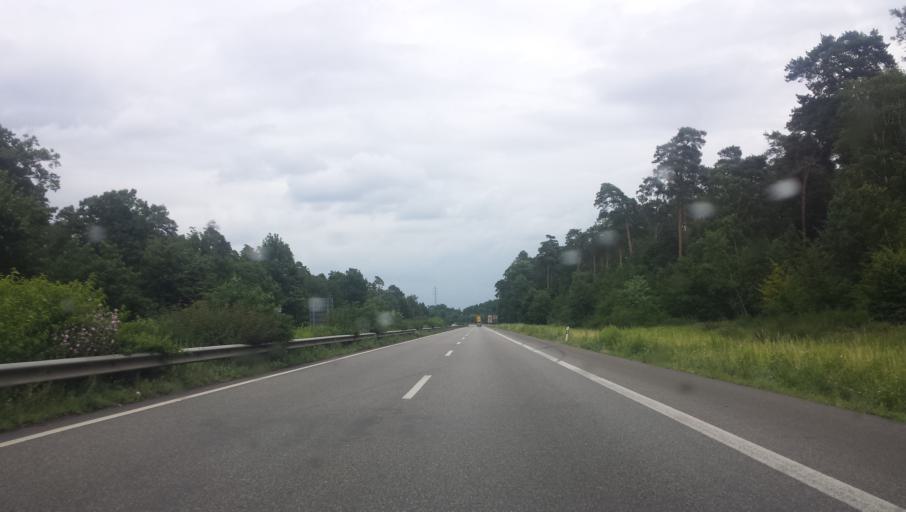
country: DE
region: Rheinland-Pfalz
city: Hordt
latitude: 49.1993
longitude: 8.3355
